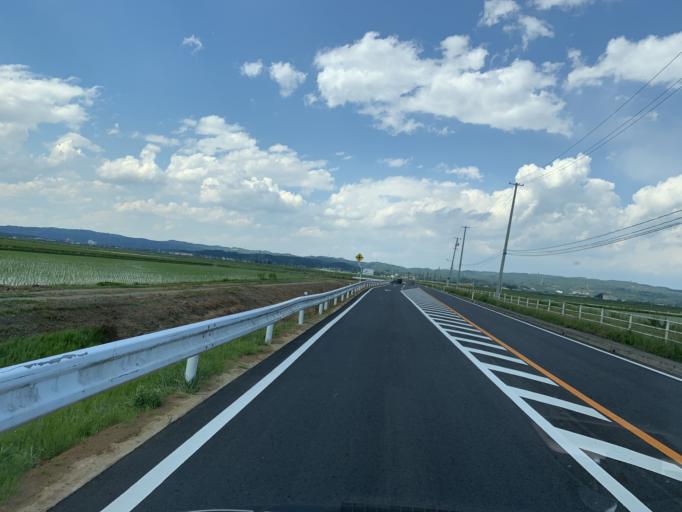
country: JP
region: Miyagi
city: Wakuya
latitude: 38.5177
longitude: 141.1277
